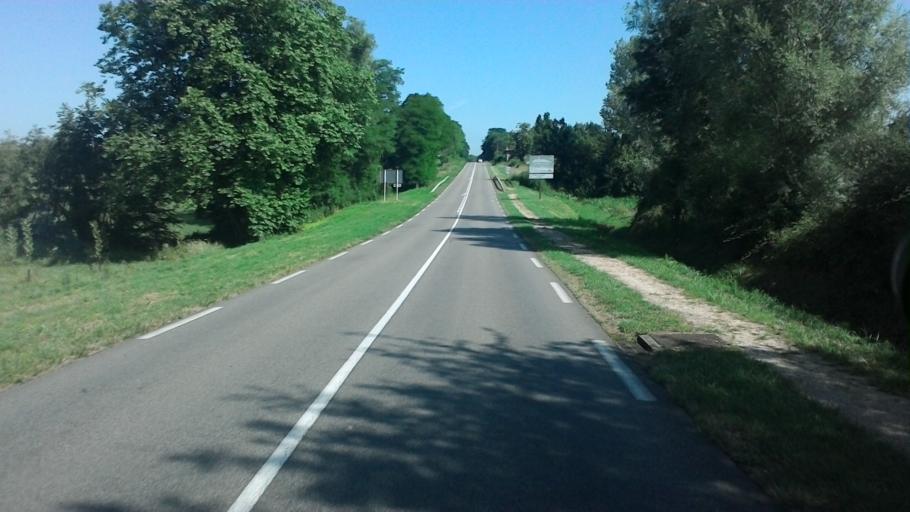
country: FR
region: Rhone-Alpes
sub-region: Departement de l'Ain
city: Saint-Trivier-de-Courtes
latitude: 46.4269
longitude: 5.0977
